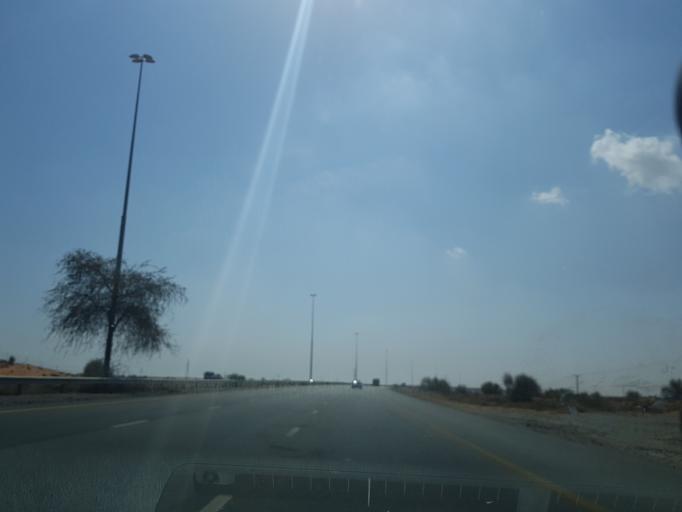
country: AE
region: Ra's al Khaymah
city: Ras al-Khaimah
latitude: 25.6831
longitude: 55.8829
